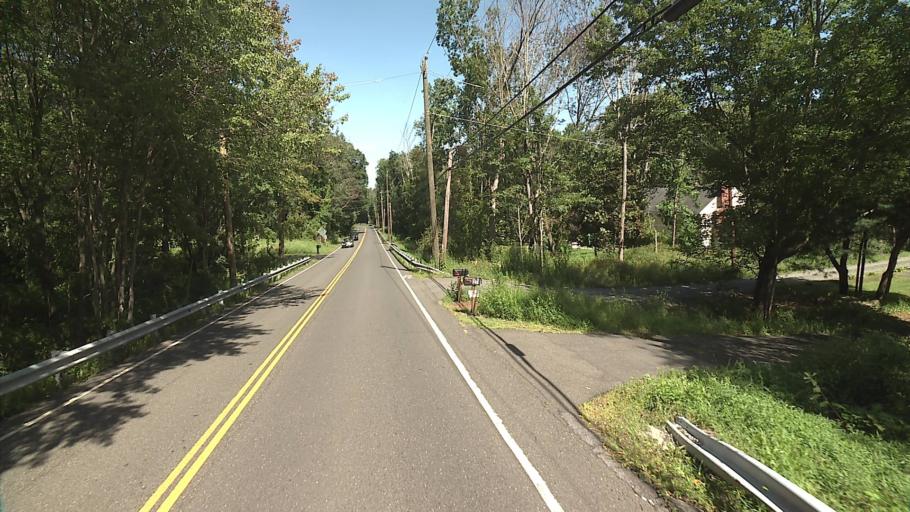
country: US
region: Connecticut
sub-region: New Haven County
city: Southbury
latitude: 41.4720
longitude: -73.1629
